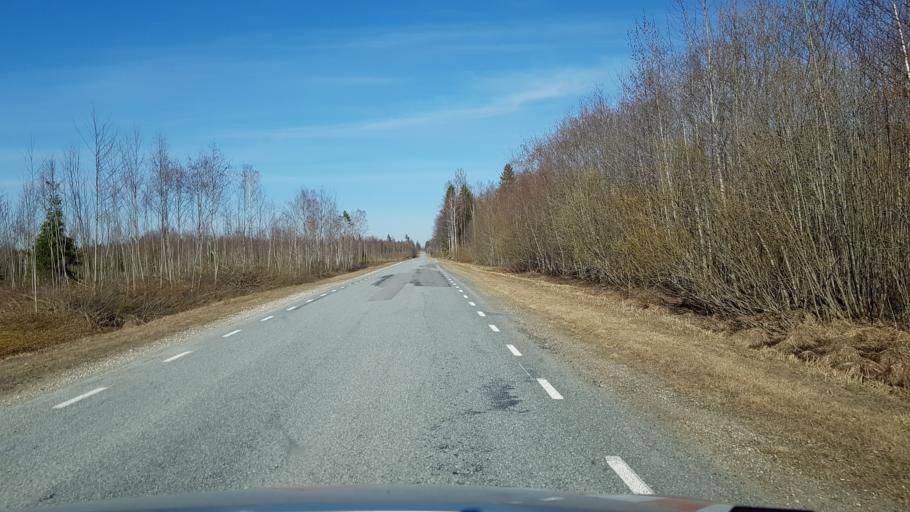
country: EE
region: Laeaene-Virumaa
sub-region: Rakke vald
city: Rakke
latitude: 59.0097
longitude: 26.3336
